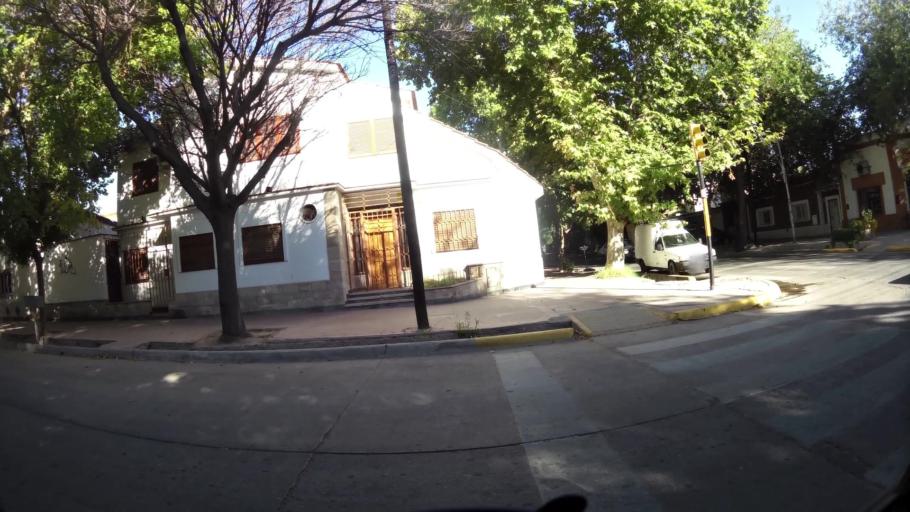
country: AR
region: Mendoza
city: Las Heras
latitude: -32.8679
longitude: -68.8361
